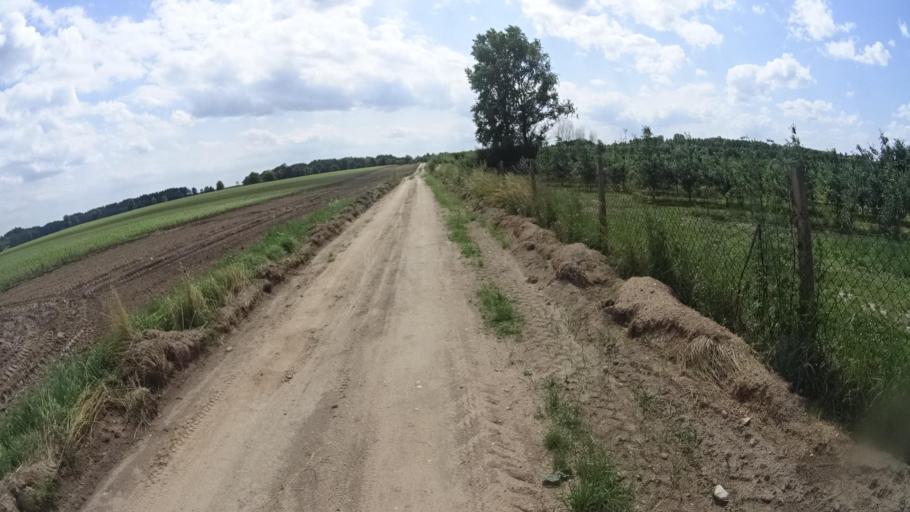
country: PL
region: Masovian Voivodeship
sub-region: Powiat grojecki
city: Goszczyn
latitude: 51.6996
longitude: 20.8242
